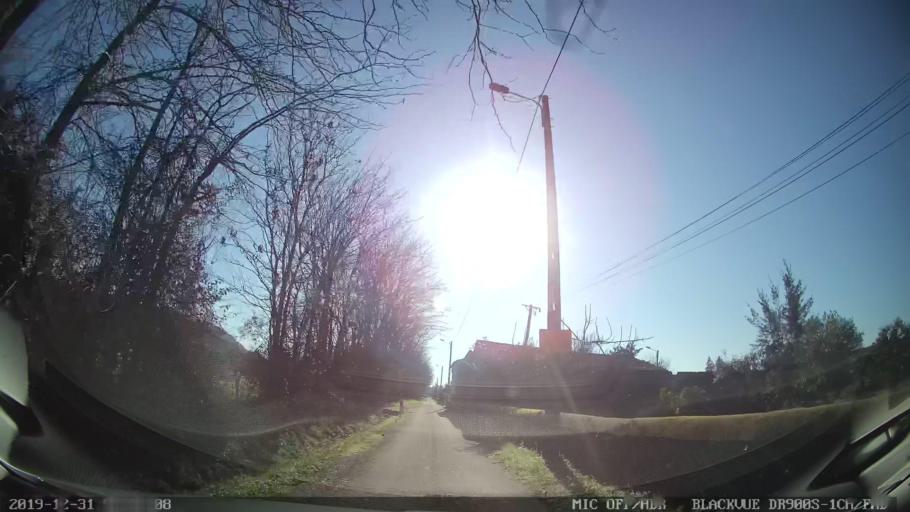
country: PT
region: Castelo Branco
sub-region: Idanha-A-Nova
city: Idanha-a-Nova
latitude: 39.9151
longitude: -7.2200
